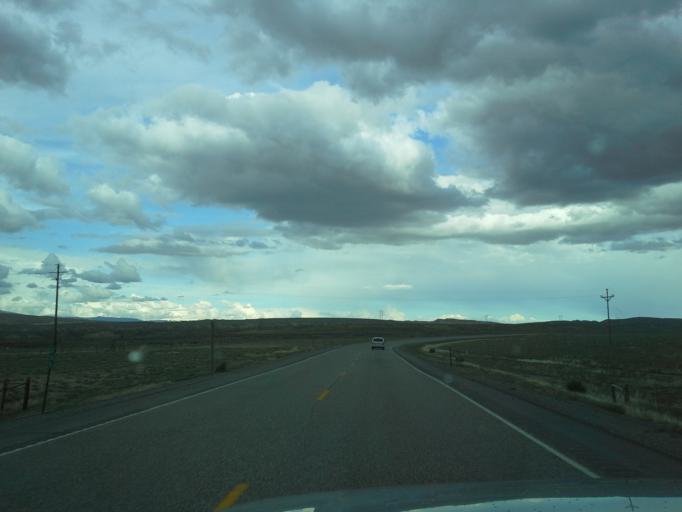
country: US
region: Wyoming
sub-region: Big Horn County
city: Lovell
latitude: 44.7815
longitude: -108.3477
